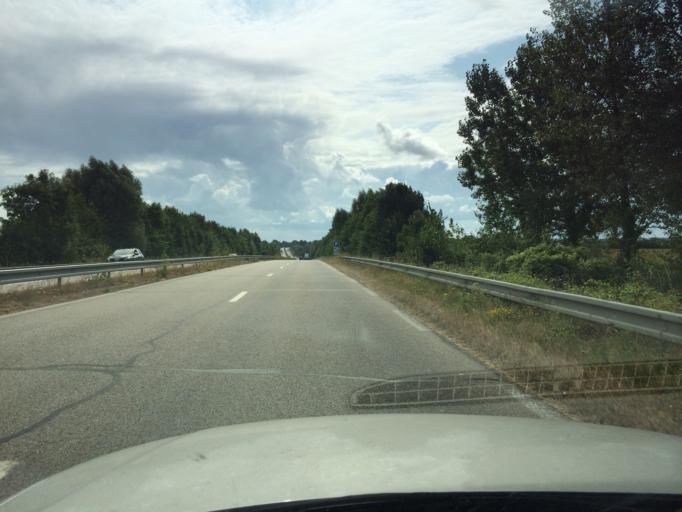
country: FR
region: Lower Normandy
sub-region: Departement de la Manche
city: Montebourg
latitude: 49.4817
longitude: -1.3882
